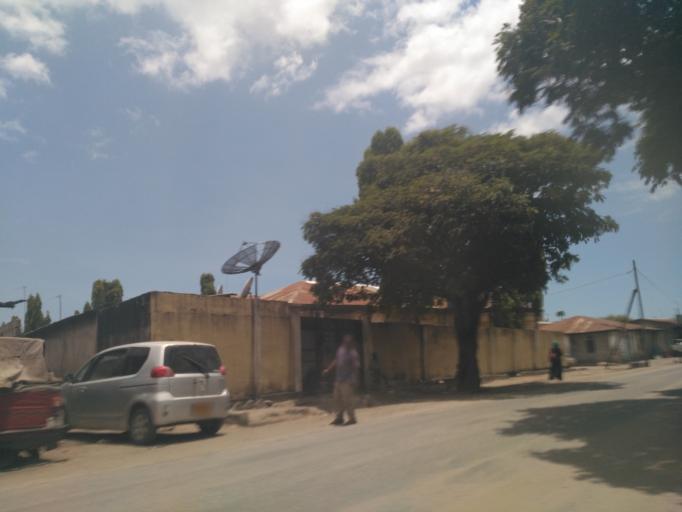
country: TZ
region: Dar es Salaam
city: Dar es Salaam
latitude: -6.8586
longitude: 39.2585
